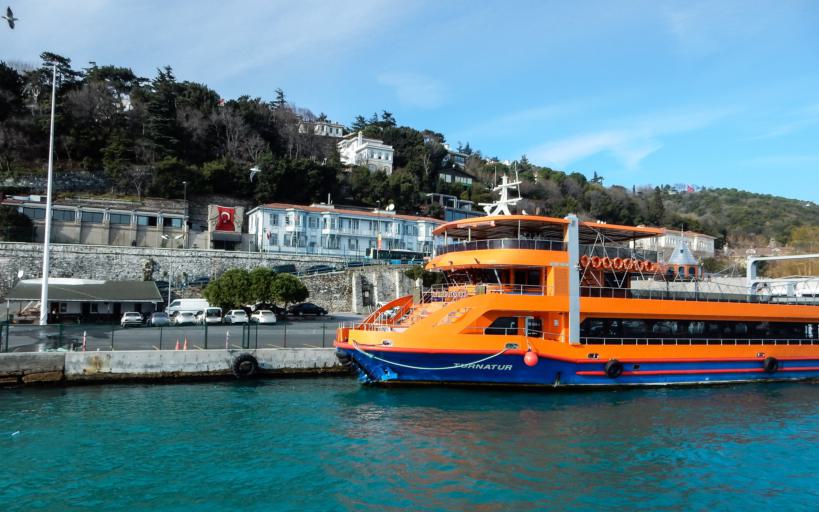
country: TR
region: Istanbul
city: UEskuedar
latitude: 41.0516
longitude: 29.0343
